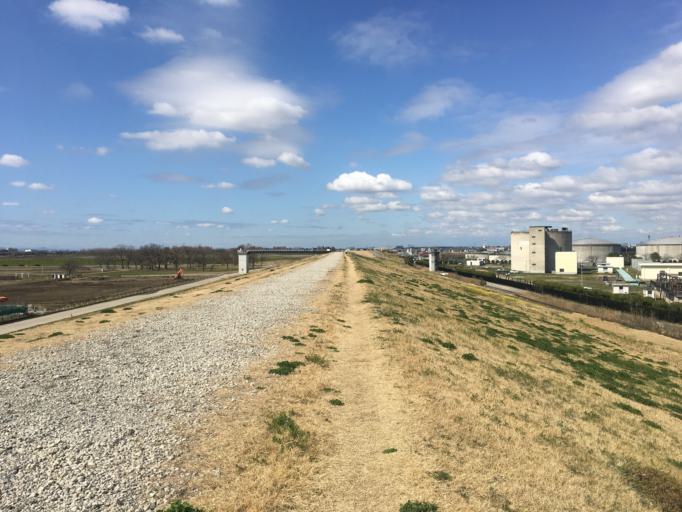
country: JP
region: Saitama
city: Shiki
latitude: 35.8736
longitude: 139.5862
